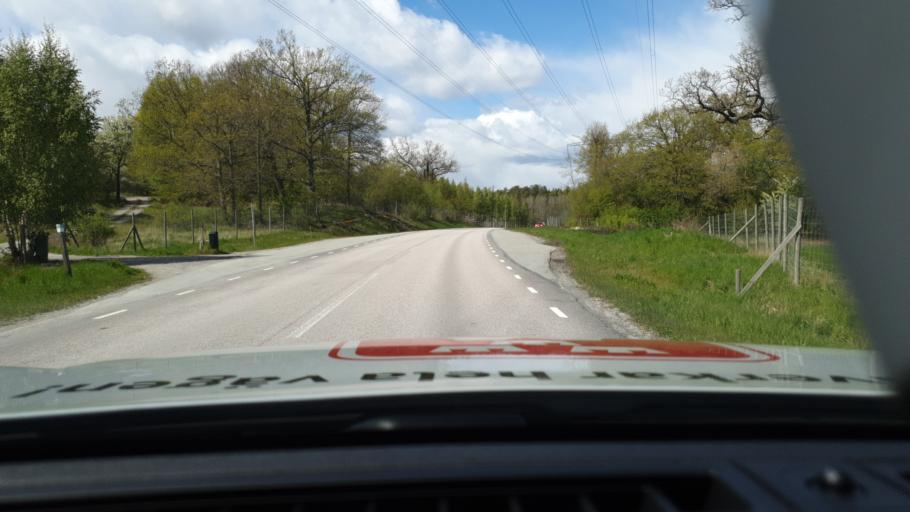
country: SE
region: Stockholm
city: Stenhamra
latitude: 59.3484
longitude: 17.6264
